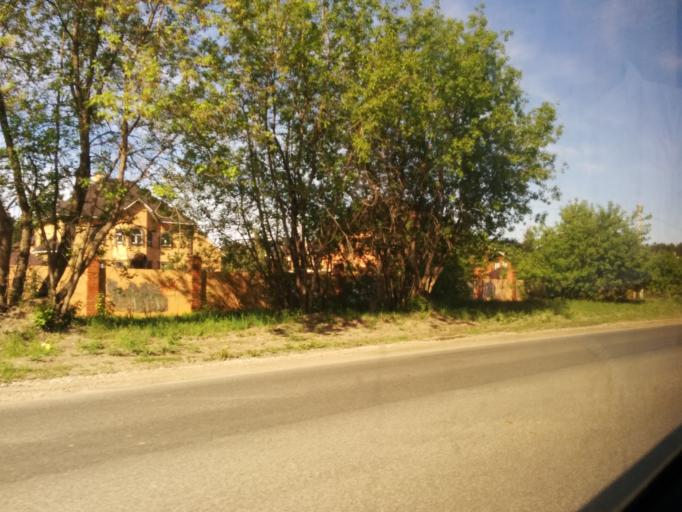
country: RU
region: Perm
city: Kondratovo
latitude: 58.0401
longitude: 56.1265
